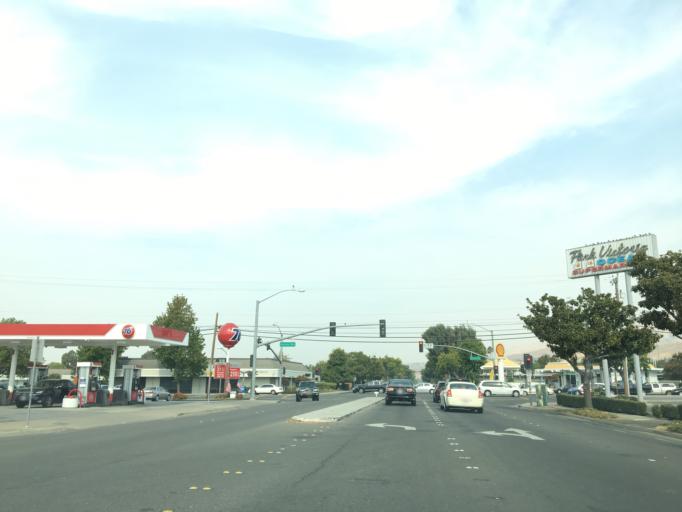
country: US
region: California
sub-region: Santa Clara County
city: Milpitas
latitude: 37.4350
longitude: -121.8840
